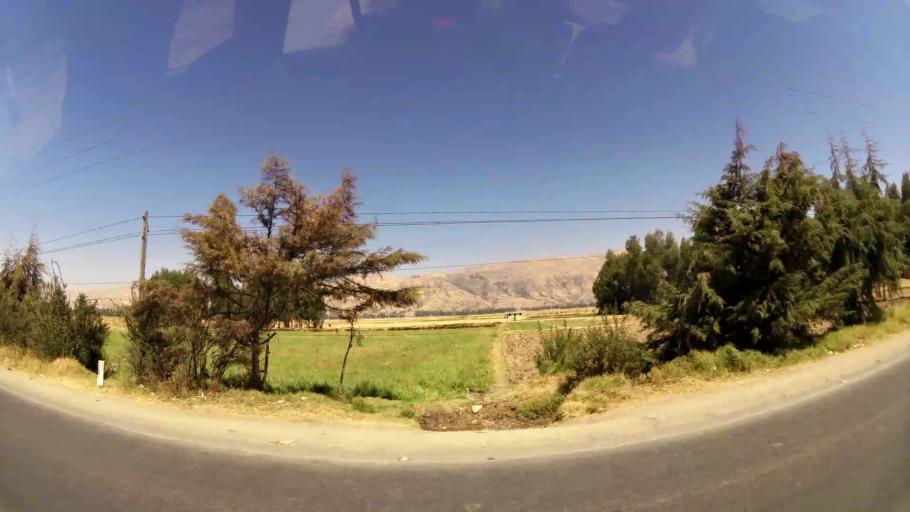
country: PE
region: Junin
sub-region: Provincia de Jauja
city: San Lorenzo
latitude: -11.8516
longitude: -75.3820
